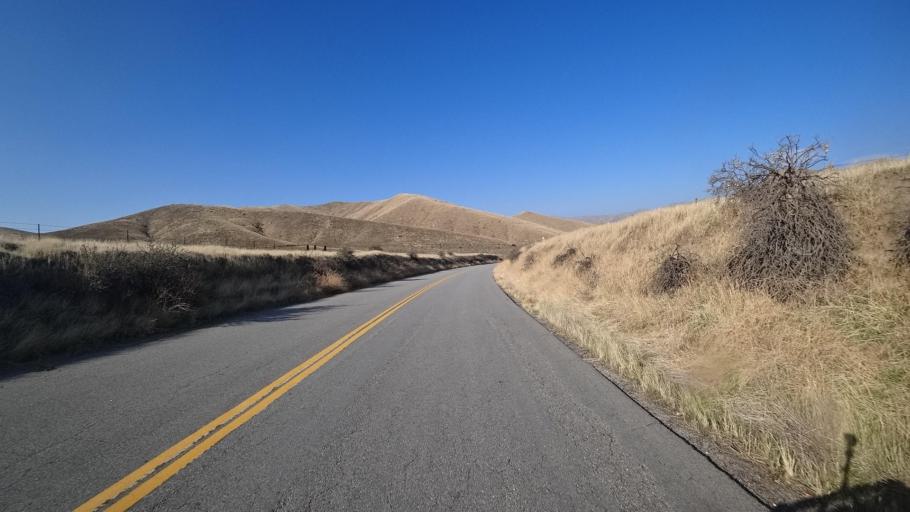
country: US
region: California
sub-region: Kern County
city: Bear Valley Springs
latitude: 35.2915
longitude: -118.6960
